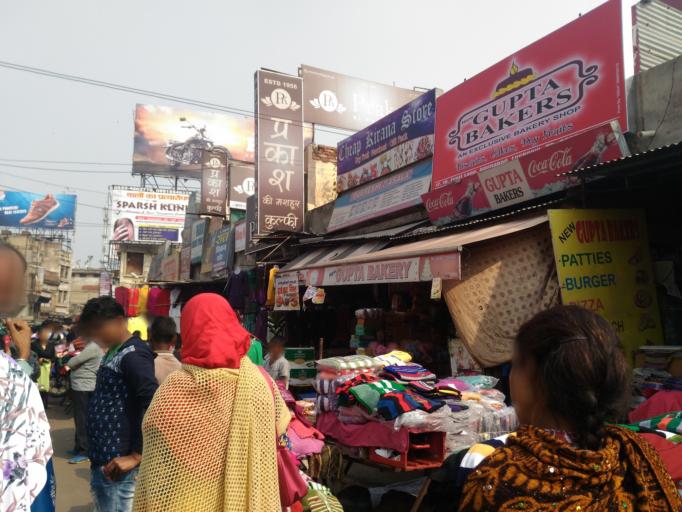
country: IN
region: Uttar Pradesh
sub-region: Lucknow District
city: Lucknow
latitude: 26.8478
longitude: 80.9275
